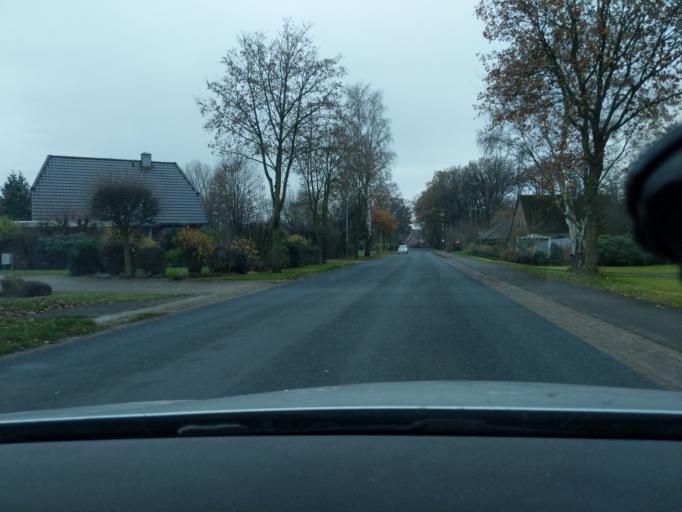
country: DE
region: Lower Saxony
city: Ahlerstedt
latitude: 53.3528
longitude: 9.4031
